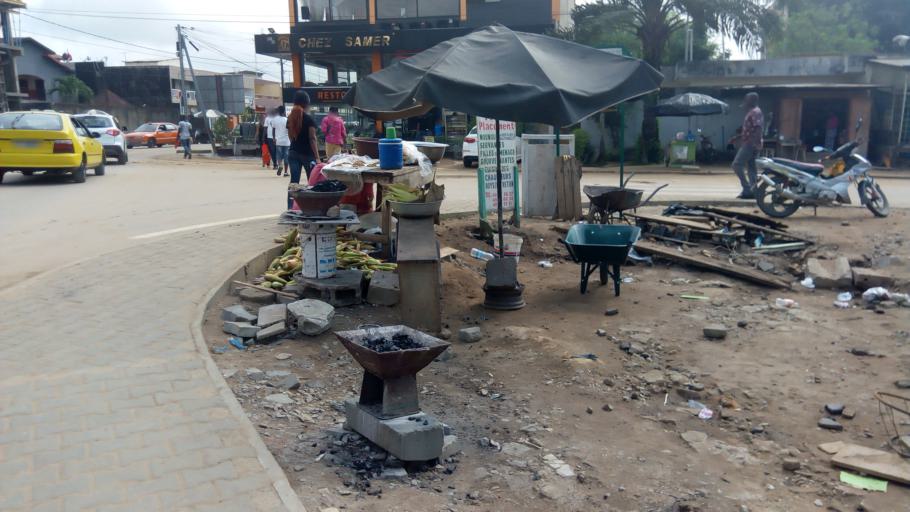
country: CI
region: Lagunes
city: Abobo
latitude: 5.3660
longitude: -3.9604
